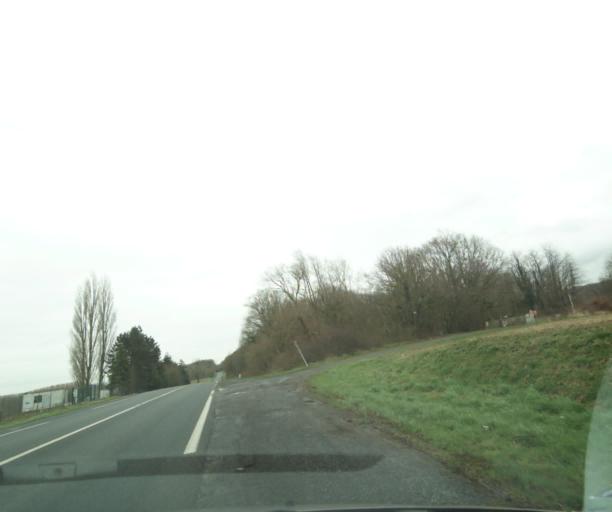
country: FR
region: Picardie
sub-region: Departement de l'Oise
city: Crisolles
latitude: 49.6089
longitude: 3.0185
